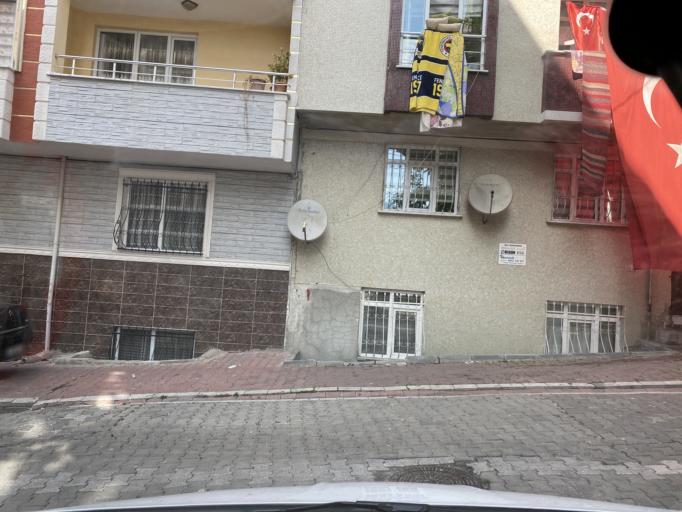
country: TR
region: Istanbul
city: Esenyurt
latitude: 41.0314
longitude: 28.6674
